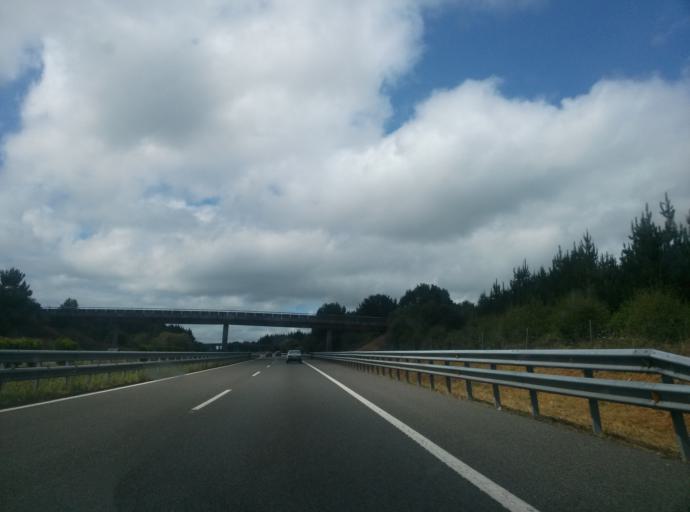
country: ES
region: Galicia
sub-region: Provincia de Lugo
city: Outeiro de Rei
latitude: 43.0838
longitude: -7.5810
